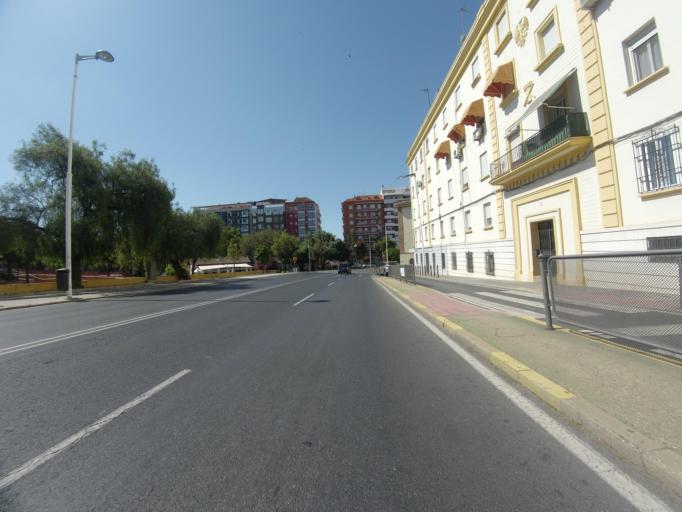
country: ES
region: Andalusia
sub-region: Provincia de Huelva
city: Huelva
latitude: 37.2553
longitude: -6.9413
